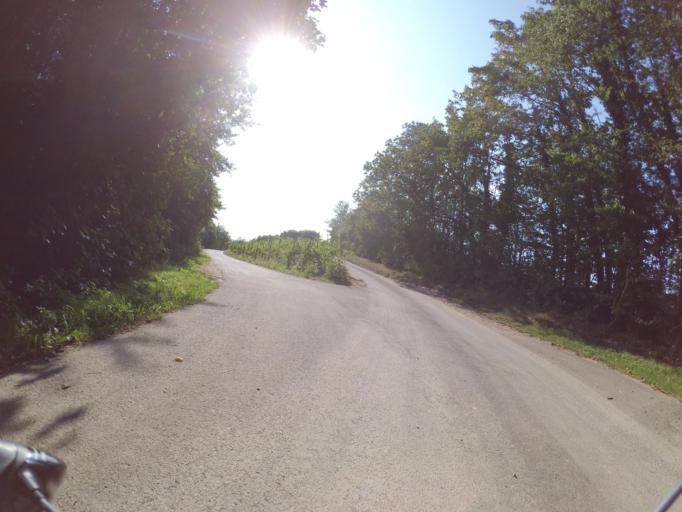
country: DE
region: Rheinland-Pfalz
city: Minheim
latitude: 49.8590
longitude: 6.9241
